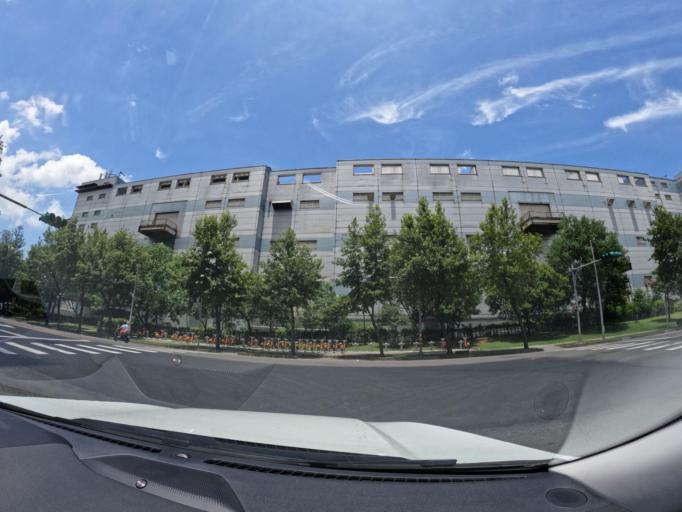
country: TW
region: Taiwan
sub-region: Taoyuan
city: Taoyuan
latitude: 25.0474
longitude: 121.3792
